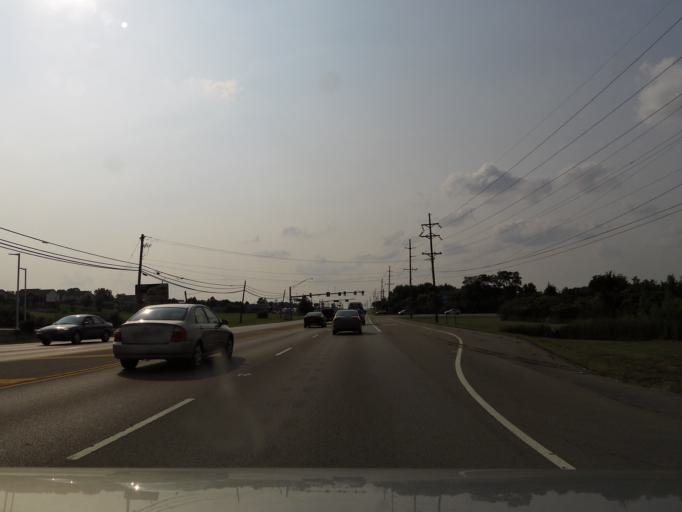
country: US
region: Ohio
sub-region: Hamilton County
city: Forest Park
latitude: 39.3233
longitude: -84.5050
